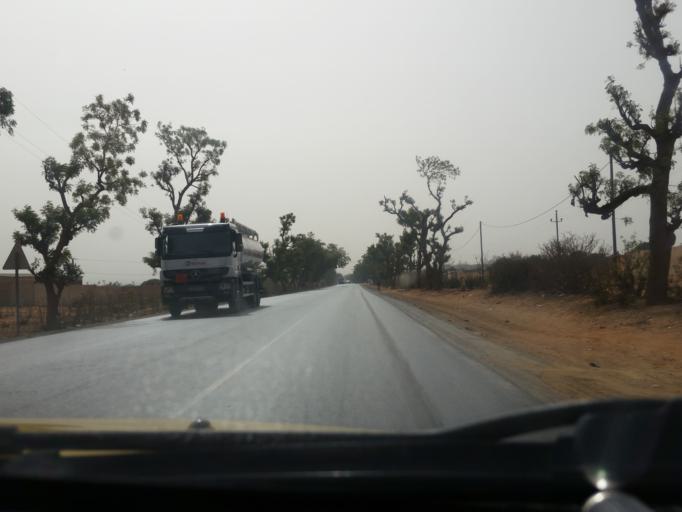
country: SN
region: Thies
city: Pout
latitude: 14.7659
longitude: -17.0971
